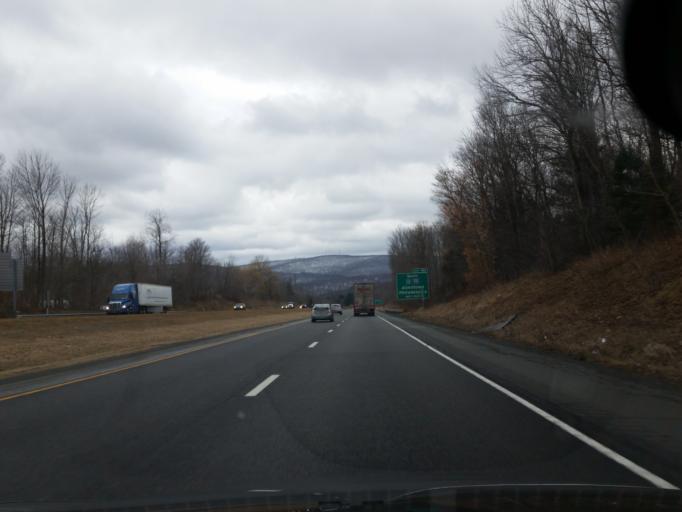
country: US
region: Pennsylvania
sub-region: Lackawanna County
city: Clarks Green
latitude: 41.5046
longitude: -75.6743
